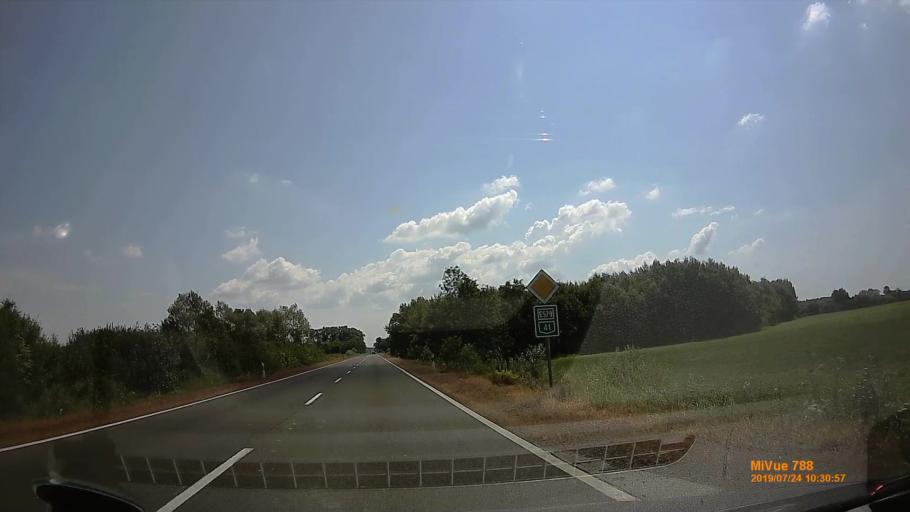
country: HU
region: Szabolcs-Szatmar-Bereg
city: Tarpa
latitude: 48.1605
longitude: 22.5010
